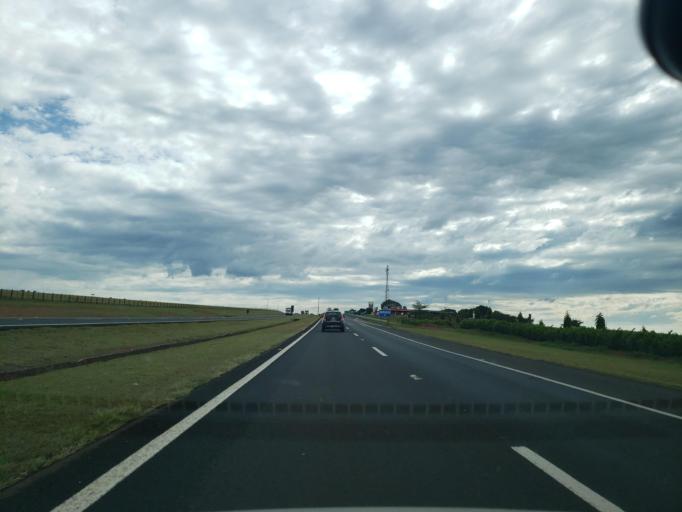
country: BR
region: Sao Paulo
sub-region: Bauru
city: Bauru
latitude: -22.1891
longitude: -49.2091
